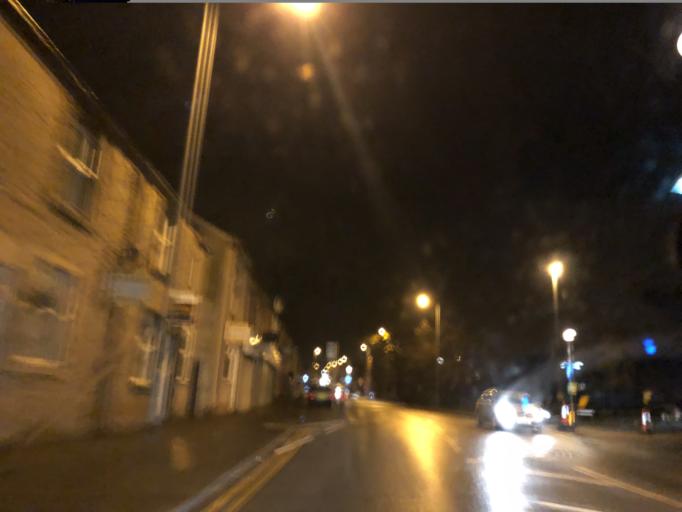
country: GB
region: England
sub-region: Borough of Oldham
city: Shaw
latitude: 53.5528
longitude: -2.0850
